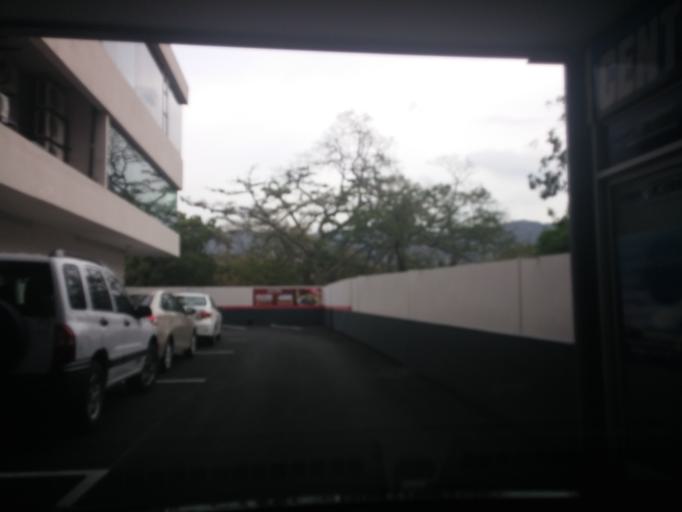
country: CR
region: San Jose
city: Santa Ana
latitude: 9.9531
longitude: -84.1960
